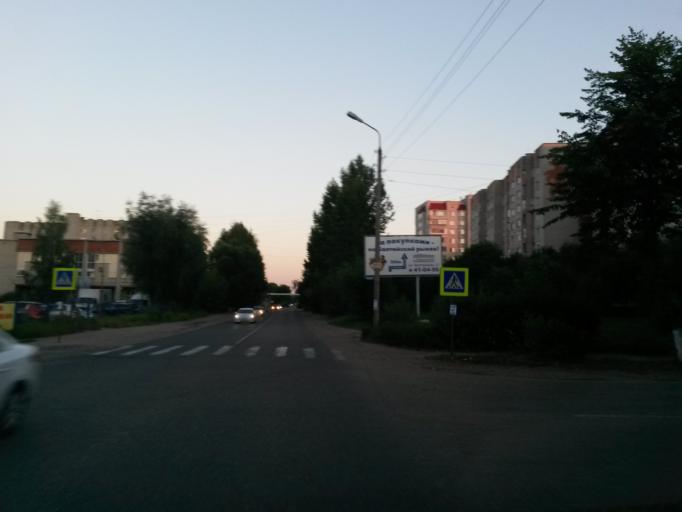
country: RU
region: Jaroslavl
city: Yaroslavl
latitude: 57.5753
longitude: 39.9289
